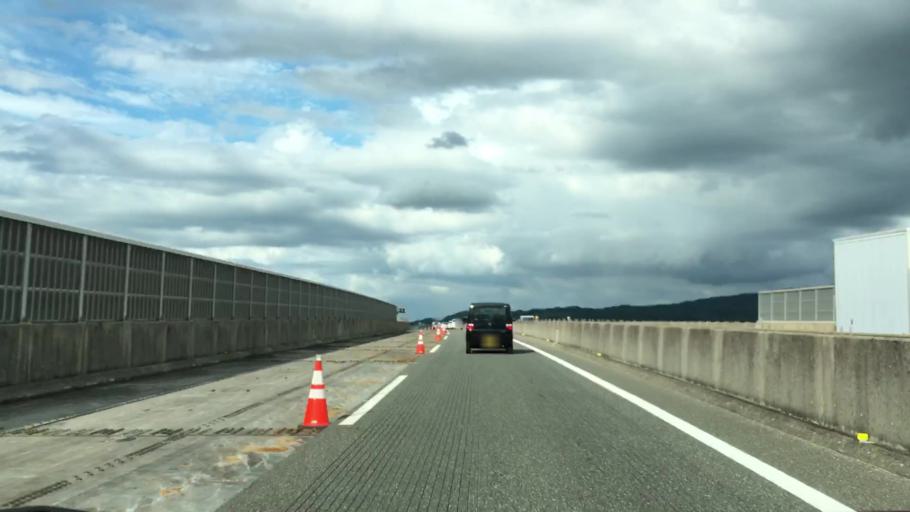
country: JP
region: Fukuoka
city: Maebaru-chuo
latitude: 33.5528
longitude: 130.2225
